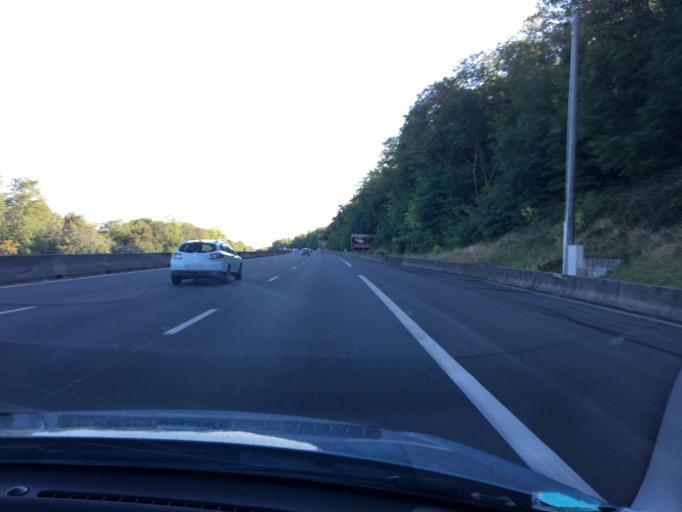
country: FR
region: Bourgogne
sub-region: Departement de Saone-et-Loire
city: Sance
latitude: 46.3446
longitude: 4.8234
